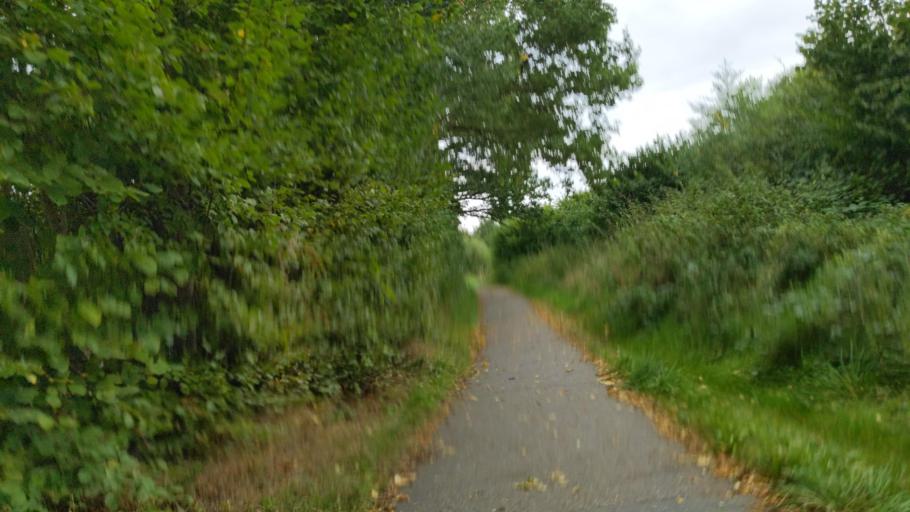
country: DE
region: Schleswig-Holstein
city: Krummesse
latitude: 53.7969
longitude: 10.6362
